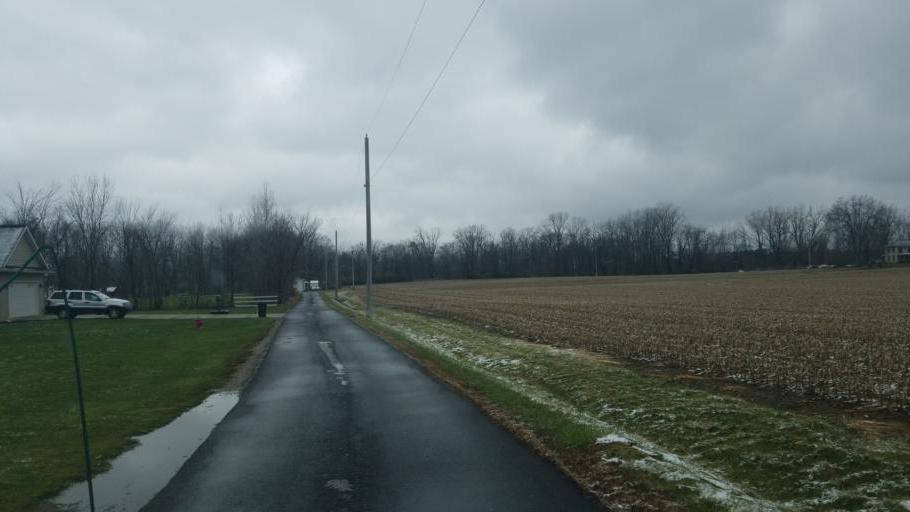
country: US
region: Ohio
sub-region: Richland County
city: Shelby
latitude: 40.9012
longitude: -82.6527
